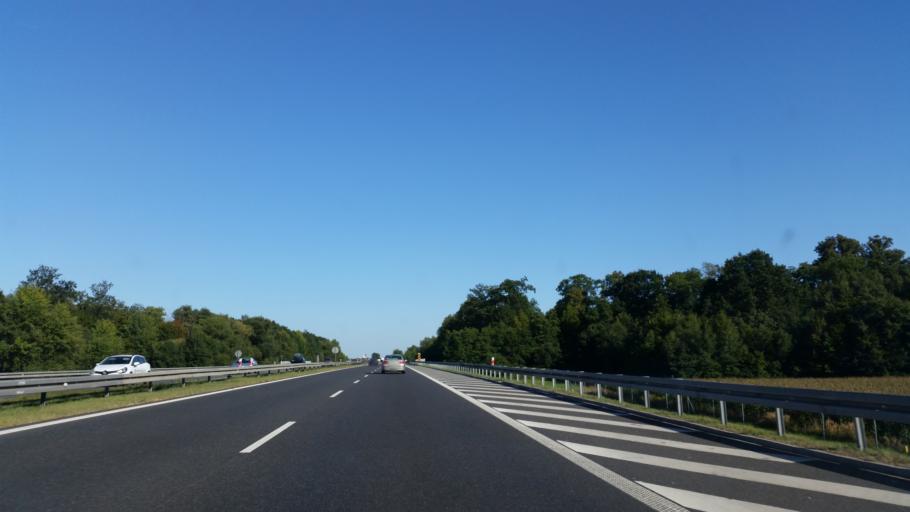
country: PL
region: Opole Voivodeship
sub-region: Powiat brzeski
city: Olszanka
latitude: 50.7305
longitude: 17.5064
